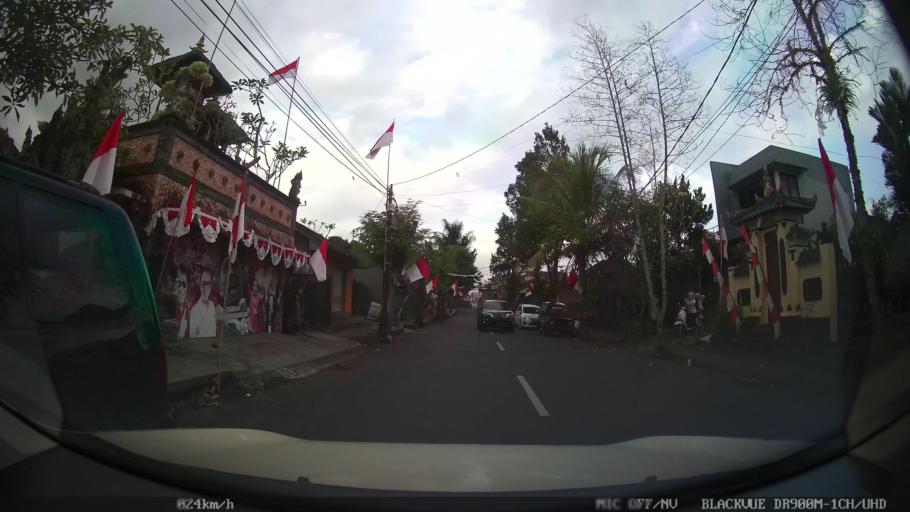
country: ID
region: Bali
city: Banjar Tegal Belodan
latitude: -8.5393
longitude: 115.1196
